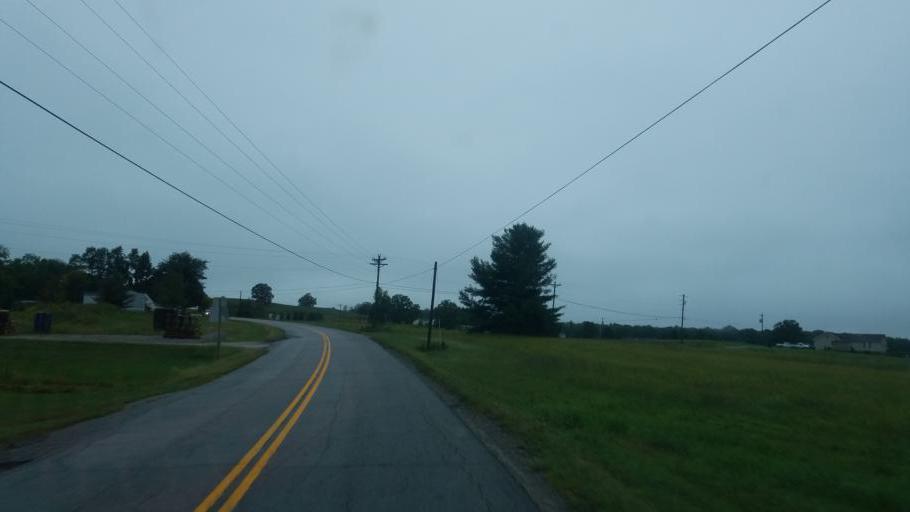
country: US
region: Kentucky
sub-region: Fleming County
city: Flemingsburg
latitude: 38.4072
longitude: -83.6433
